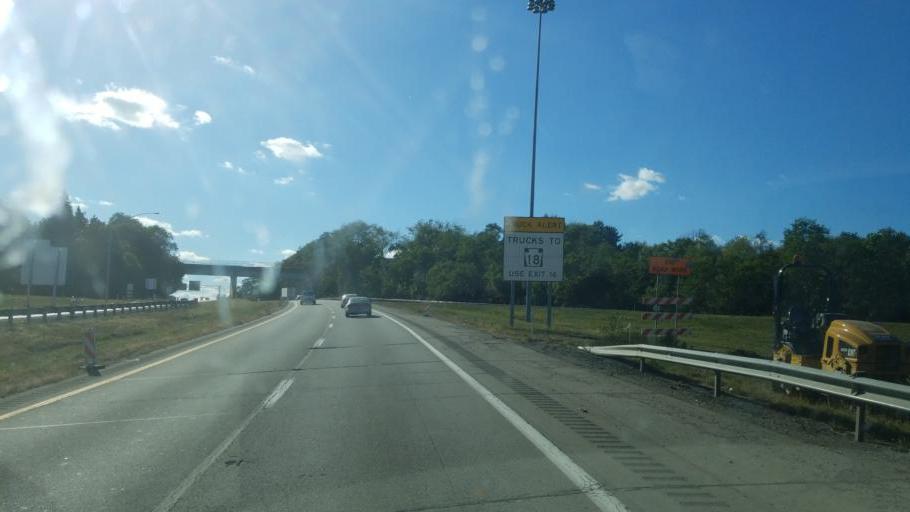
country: US
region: Pennsylvania
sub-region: Washington County
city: Washington
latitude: 40.1886
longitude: -80.2473
